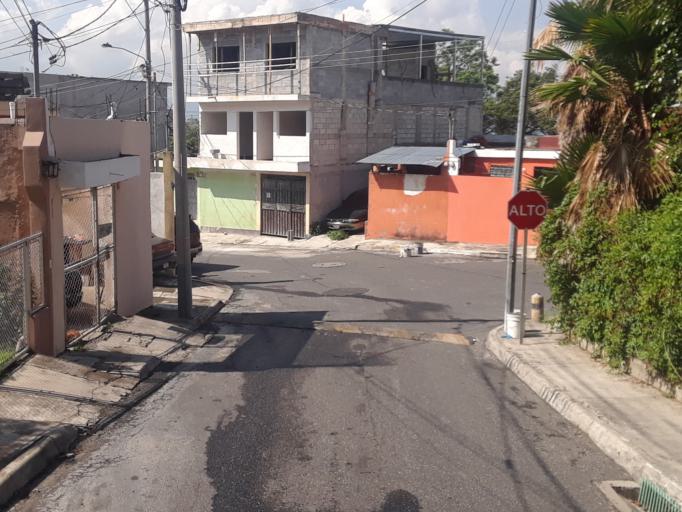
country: GT
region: Guatemala
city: Petapa
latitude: 14.5352
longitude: -90.5532
